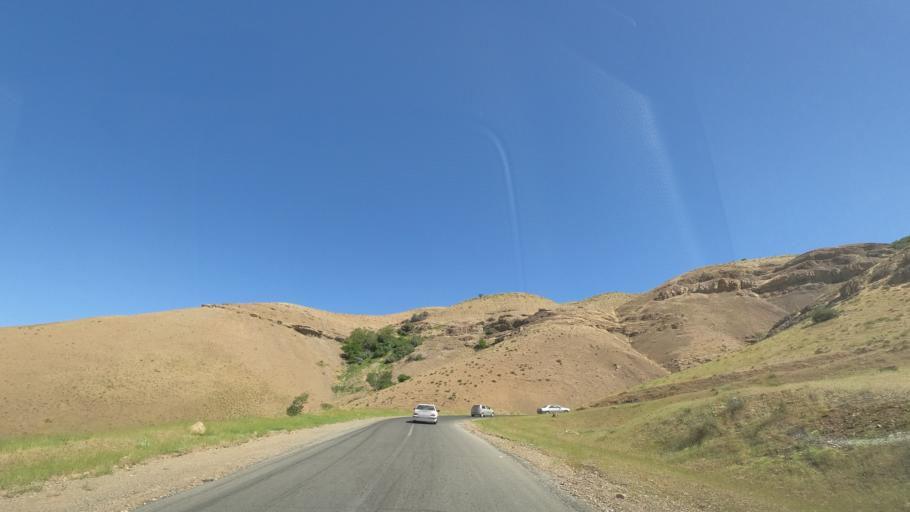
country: IR
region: Alborz
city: Karaj
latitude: 35.9264
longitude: 51.0989
